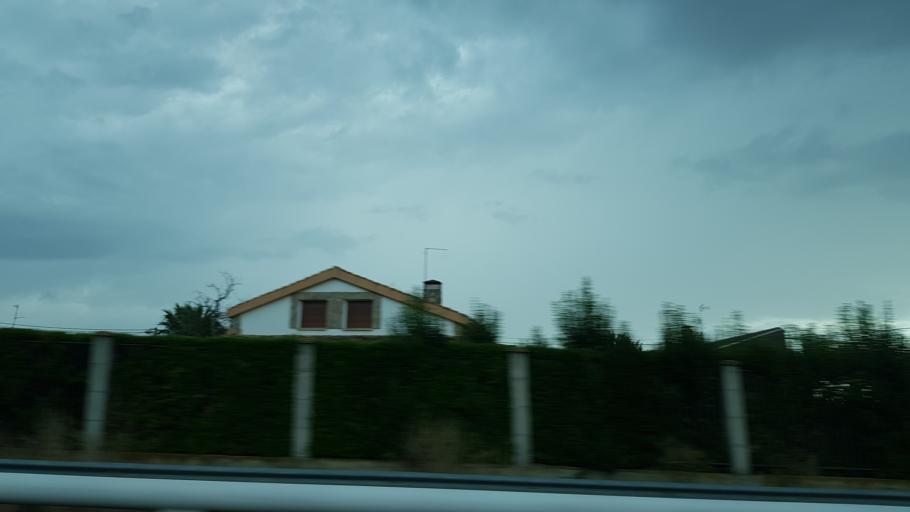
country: ES
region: La Rioja
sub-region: Provincia de La Rioja
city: Lardero
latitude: 42.3980
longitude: -2.4719
